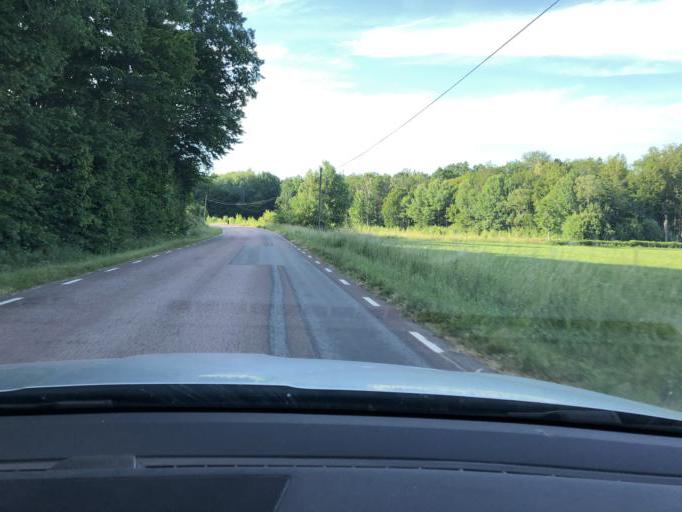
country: SE
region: Blekinge
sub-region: Solvesborgs Kommun
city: Soelvesborg
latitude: 56.1404
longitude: 14.6068
